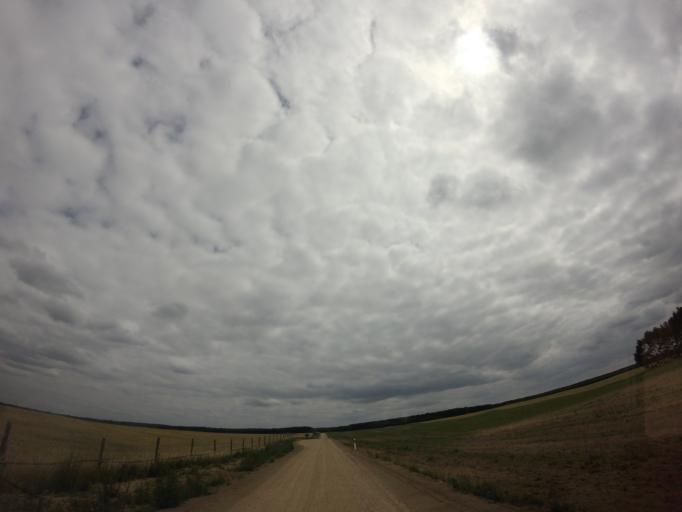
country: PL
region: Lubusz
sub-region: Powiat strzelecko-drezdenecki
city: Zwierzyn
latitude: 52.8819
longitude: 15.6045
